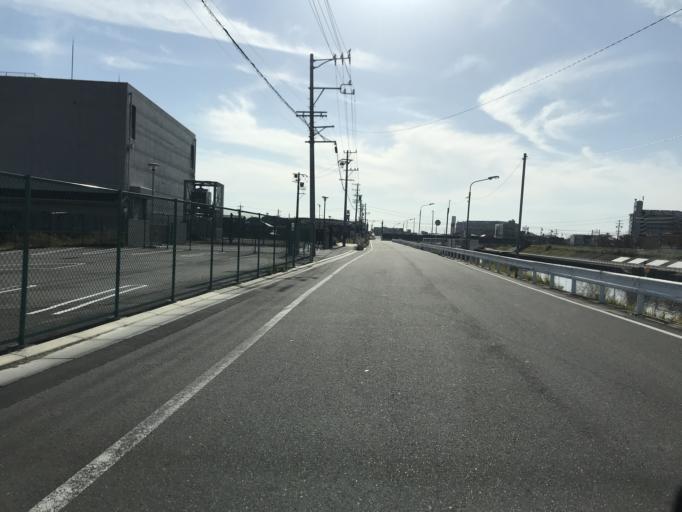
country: JP
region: Aichi
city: Nagoya-shi
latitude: 35.1981
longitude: 136.8534
